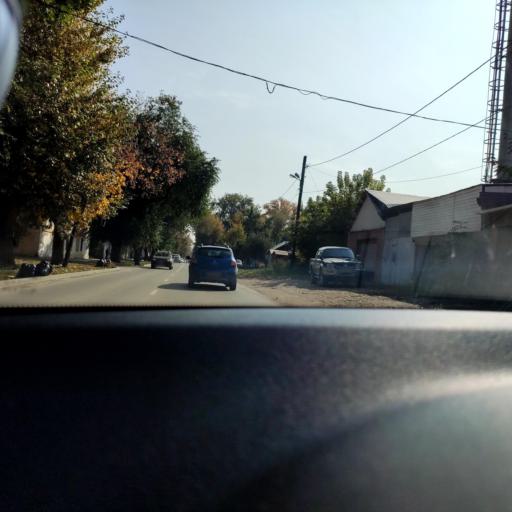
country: RU
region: Samara
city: Samara
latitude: 53.2249
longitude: 50.2520
